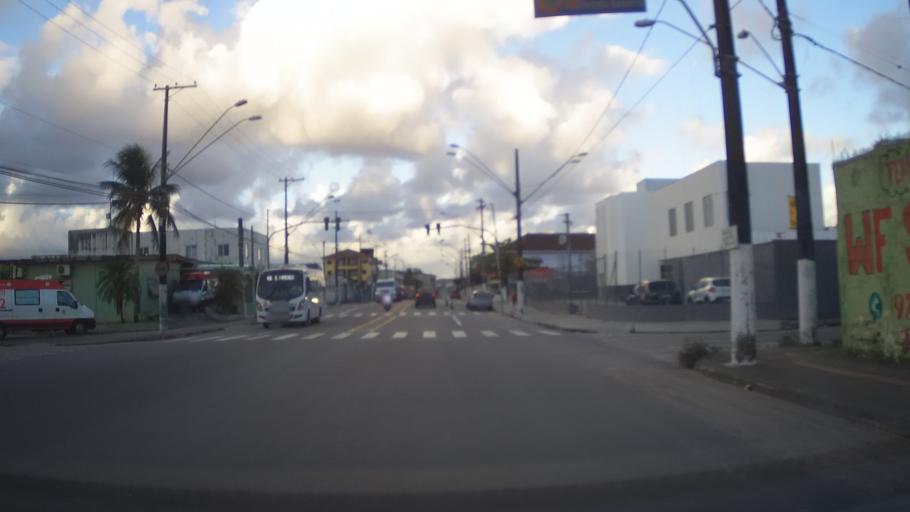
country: BR
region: Sao Paulo
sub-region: Sao Vicente
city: Sao Vicente
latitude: -23.9508
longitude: -46.4072
